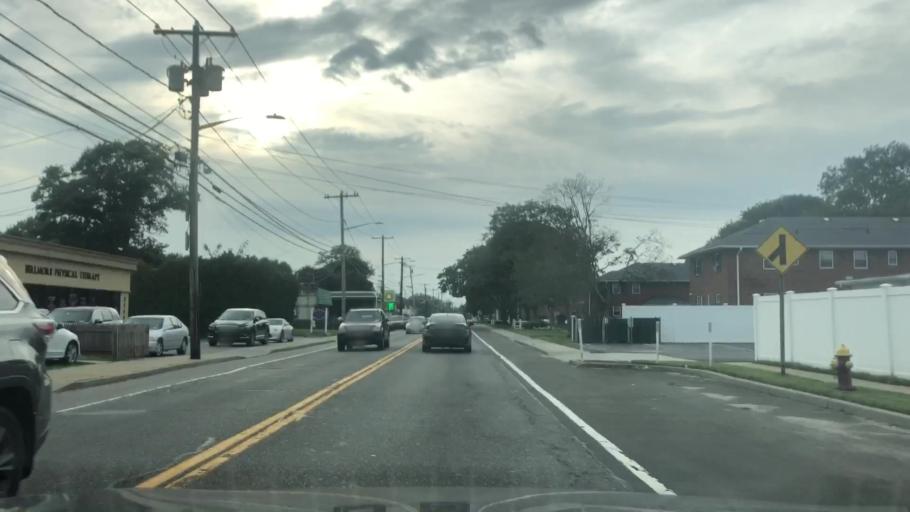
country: US
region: New York
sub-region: Nassau County
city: North Bellmore
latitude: 40.6914
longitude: -73.5367
